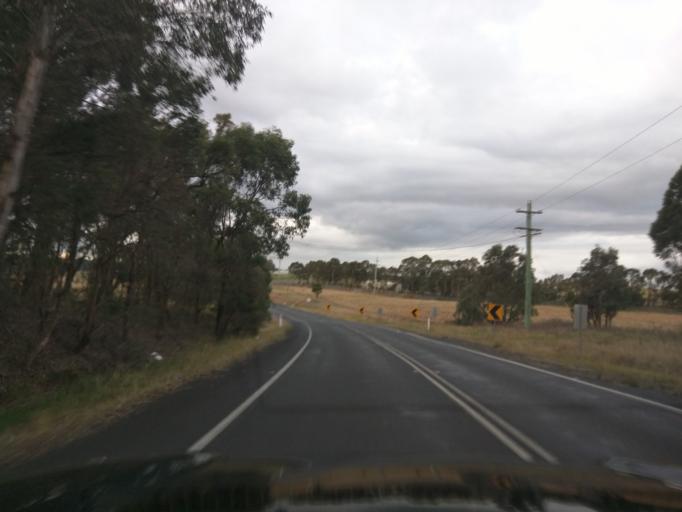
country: AU
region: New South Wales
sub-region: Wollondilly
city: Douglas Park
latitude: -34.2207
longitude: 150.7689
